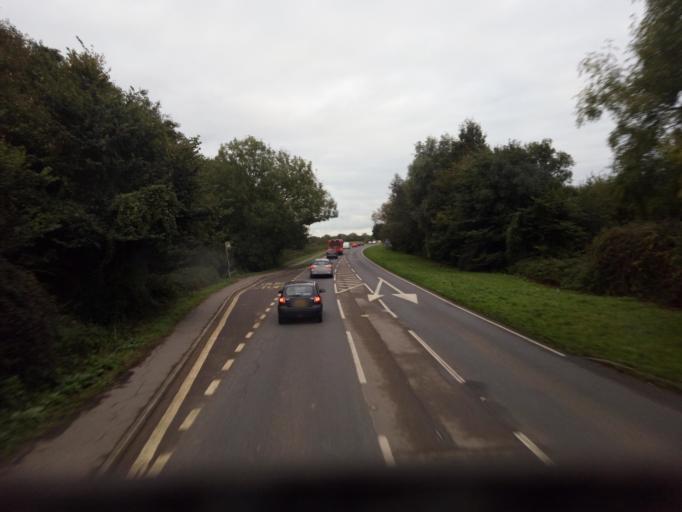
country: GB
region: England
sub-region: West Sussex
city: Boxgrove
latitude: 50.8195
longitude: -0.7158
